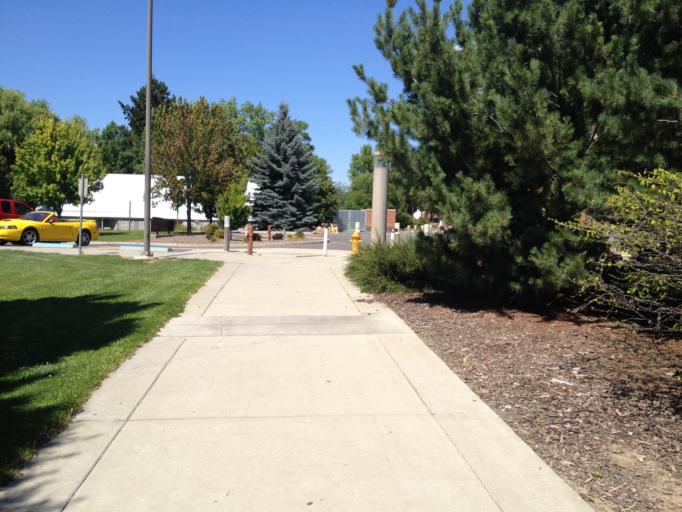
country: US
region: Washington
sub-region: Kittitas County
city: Ellensburg
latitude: 47.0035
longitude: -120.5423
